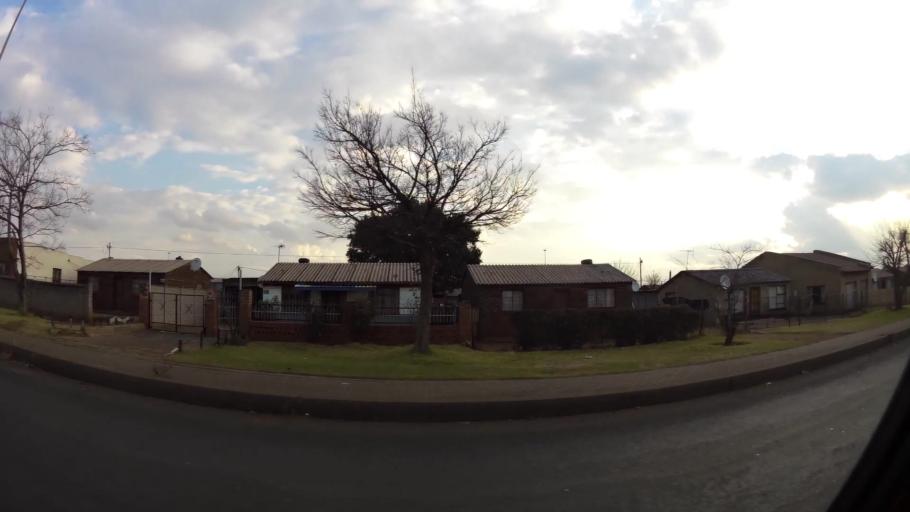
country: ZA
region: Gauteng
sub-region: City of Johannesburg Metropolitan Municipality
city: Orange Farm
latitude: -26.5788
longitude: 27.8416
